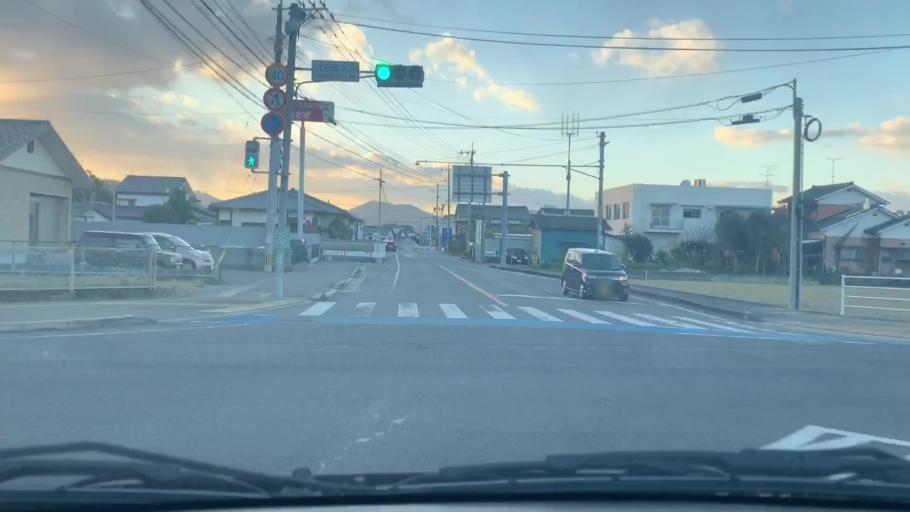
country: JP
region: Saga Prefecture
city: Kashima
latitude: 33.1866
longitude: 130.1410
